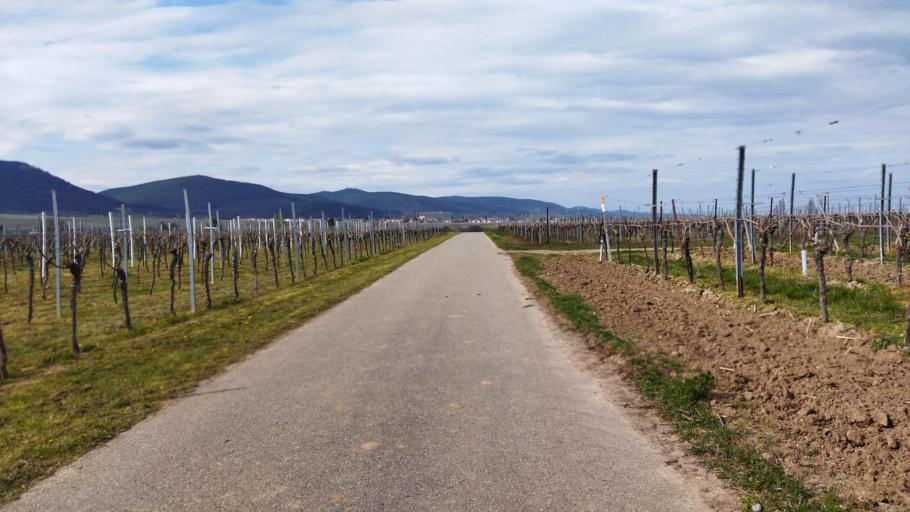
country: DE
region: Rheinland-Pfalz
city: Roschbach
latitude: 49.2527
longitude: 8.1118
